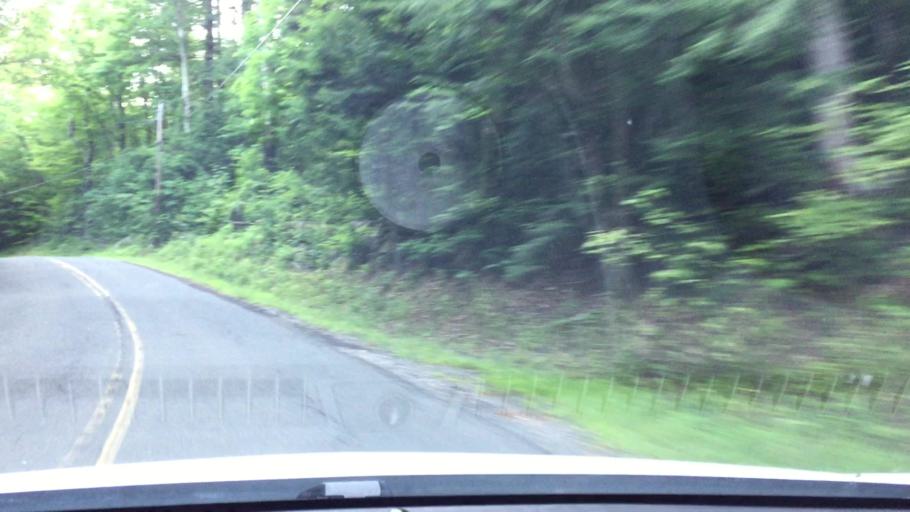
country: US
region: Massachusetts
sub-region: Berkshire County
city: Otis
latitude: 42.2415
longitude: -73.1124
